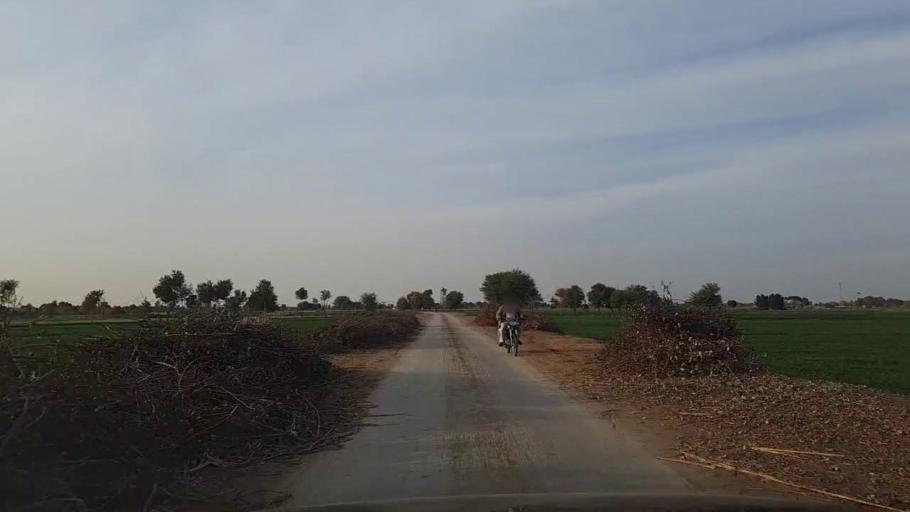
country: PK
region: Sindh
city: Jam Sahib
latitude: 26.4330
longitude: 68.5647
